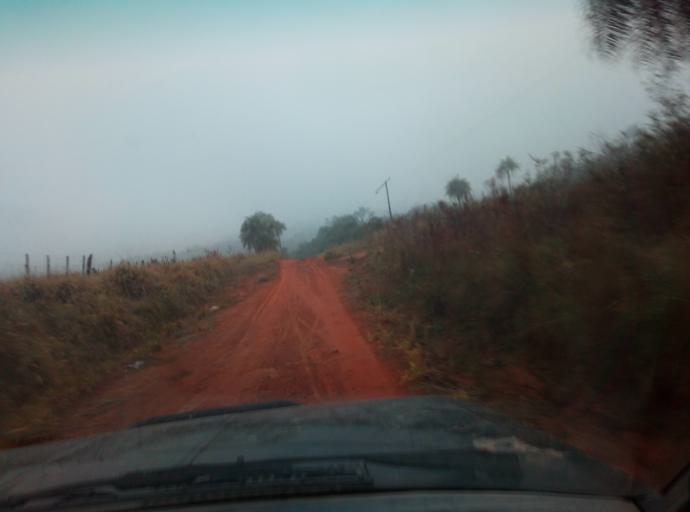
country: PY
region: Caaguazu
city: Doctor Cecilio Baez
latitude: -25.1583
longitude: -56.2540
